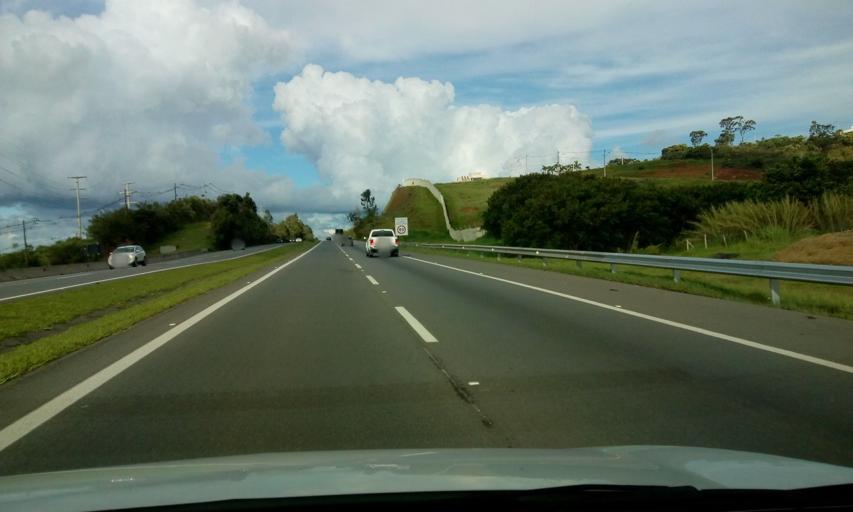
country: BR
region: Sao Paulo
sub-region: Jundiai
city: Jundiai
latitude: -23.1588
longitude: -46.8973
